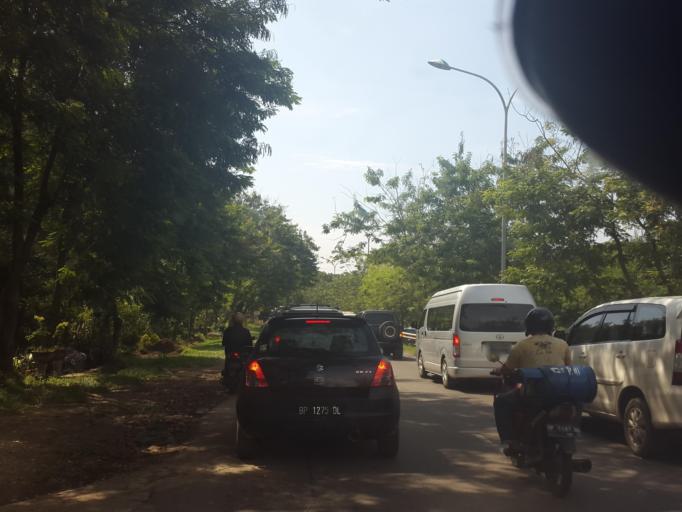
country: SG
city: Singapore
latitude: 1.1316
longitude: 104.0296
